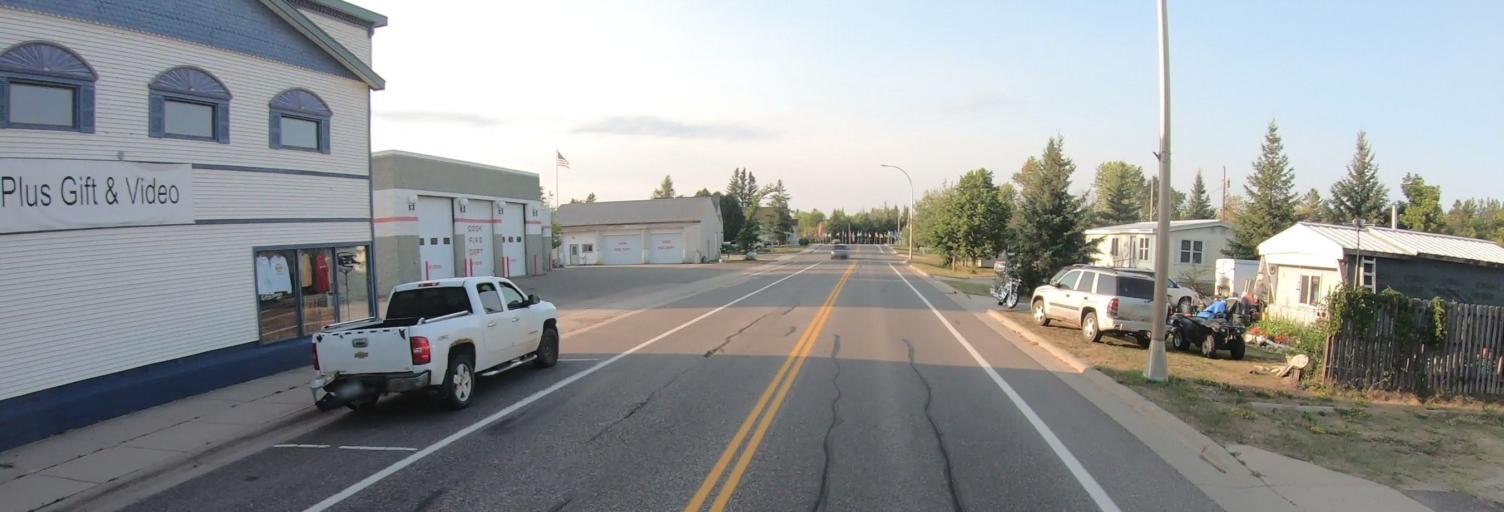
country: US
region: Minnesota
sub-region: Saint Louis County
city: Mountain Iron
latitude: 47.8507
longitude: -92.6817
